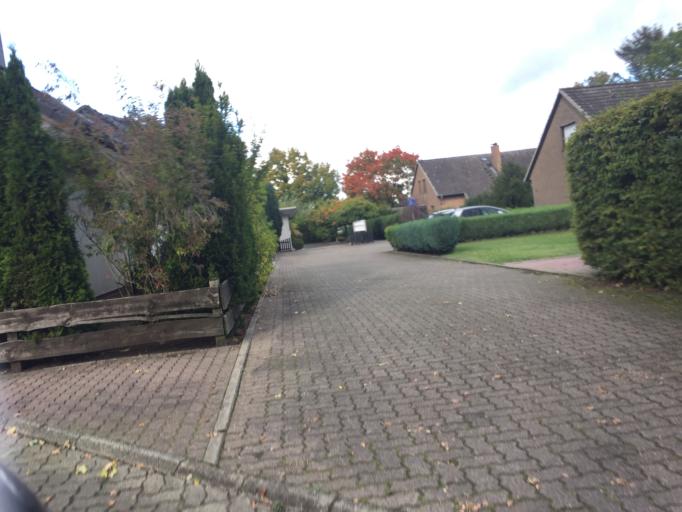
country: DE
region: Schleswig-Holstein
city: Ottenbuttel
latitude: 53.9531
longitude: 9.5008
